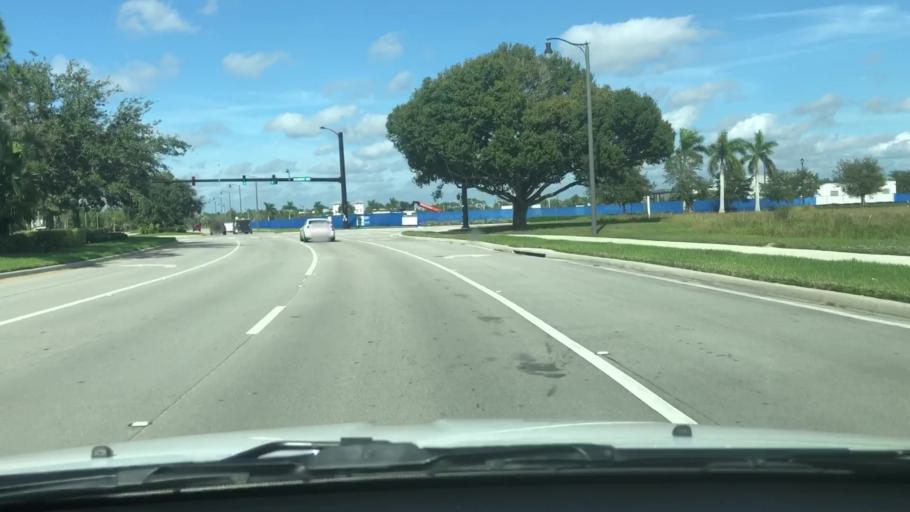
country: US
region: Florida
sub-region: Saint Lucie County
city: Port Saint Lucie
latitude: 27.2726
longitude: -80.4301
